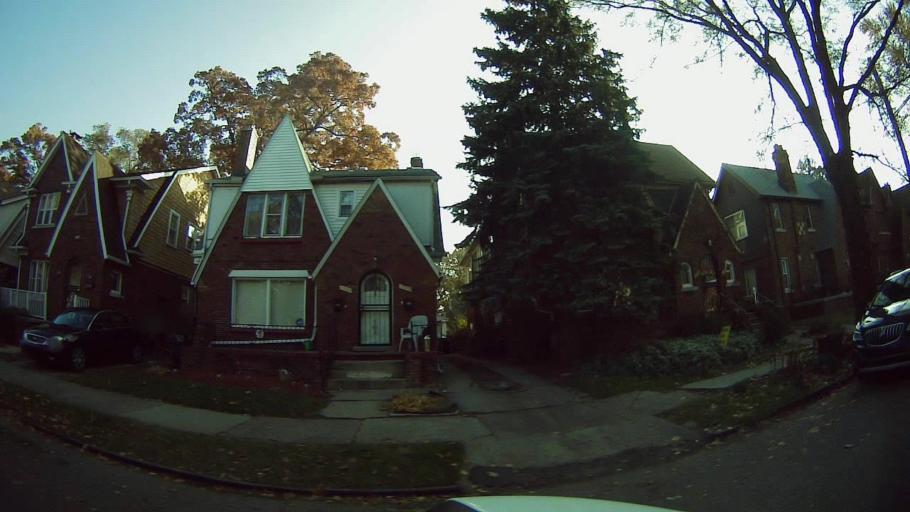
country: US
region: Michigan
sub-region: Oakland County
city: Ferndale
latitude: 42.4199
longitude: -83.1400
